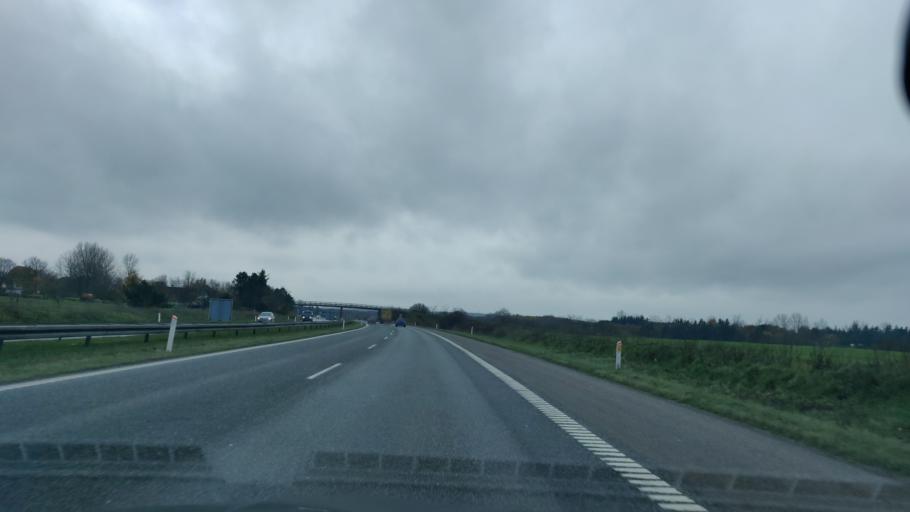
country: DK
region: North Denmark
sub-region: Alborg Kommune
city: Svenstrup
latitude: 56.9842
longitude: 9.8823
